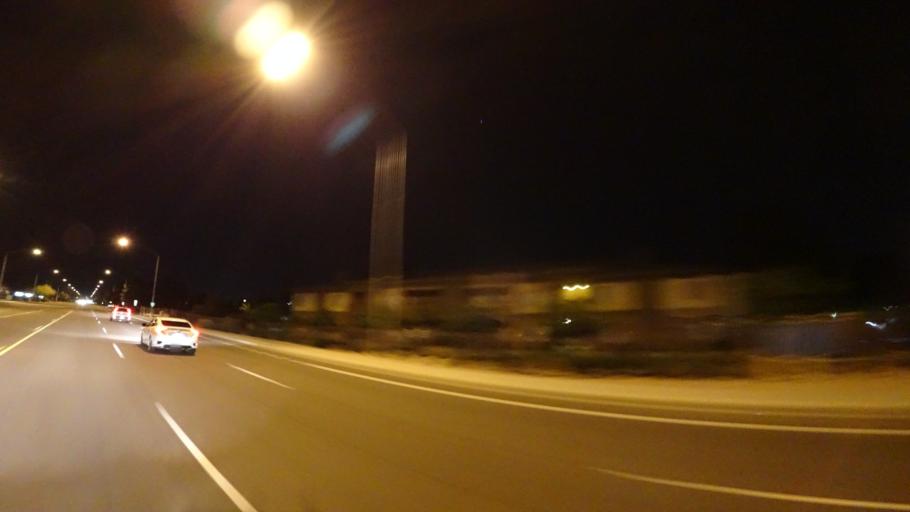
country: US
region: Arizona
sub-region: Maricopa County
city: Gilbert
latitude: 33.3938
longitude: -111.7161
